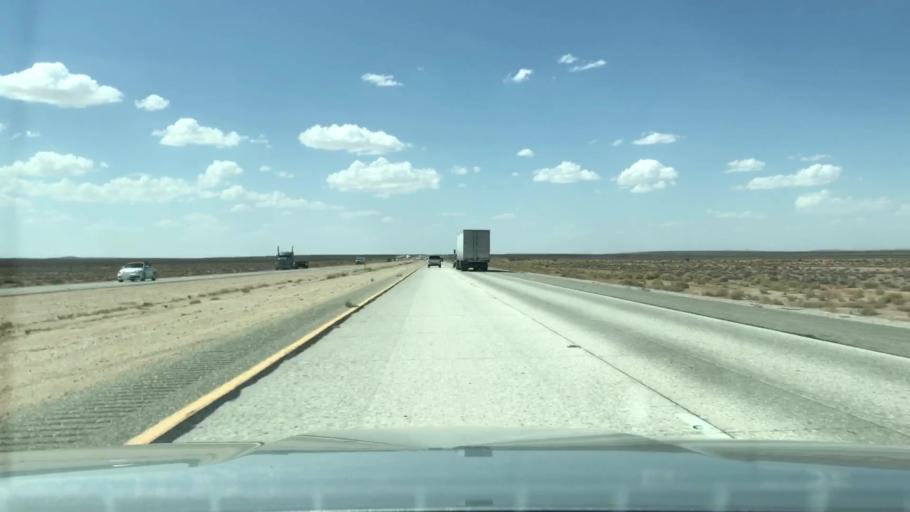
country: US
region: California
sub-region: San Bernardino County
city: Lenwood
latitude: 34.9362
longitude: -117.3768
